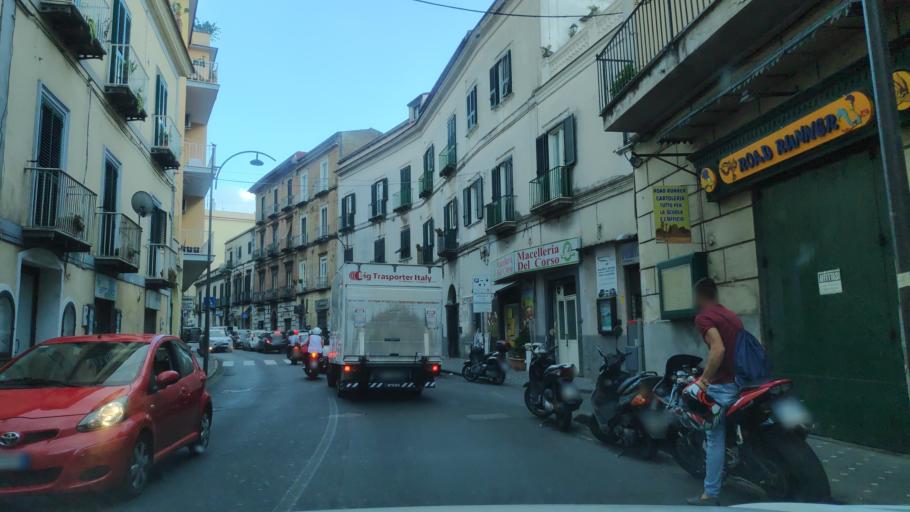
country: IT
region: Campania
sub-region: Provincia di Napoli
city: Meta
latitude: 40.6385
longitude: 14.4187
